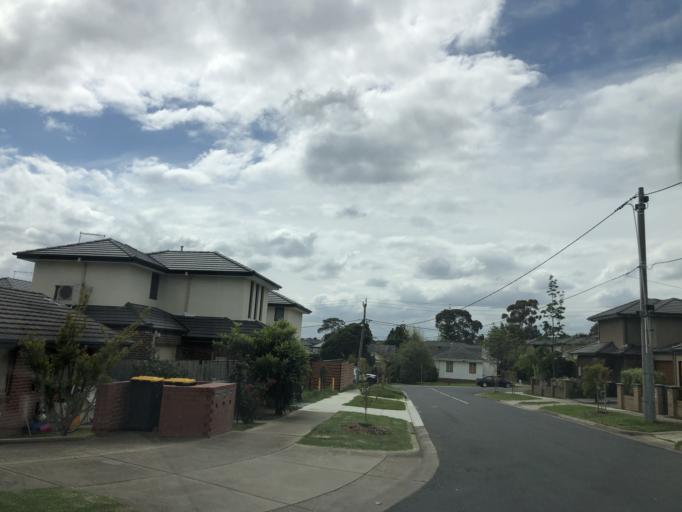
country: AU
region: Victoria
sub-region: Monash
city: Ashwood
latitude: -37.8727
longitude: 145.1011
